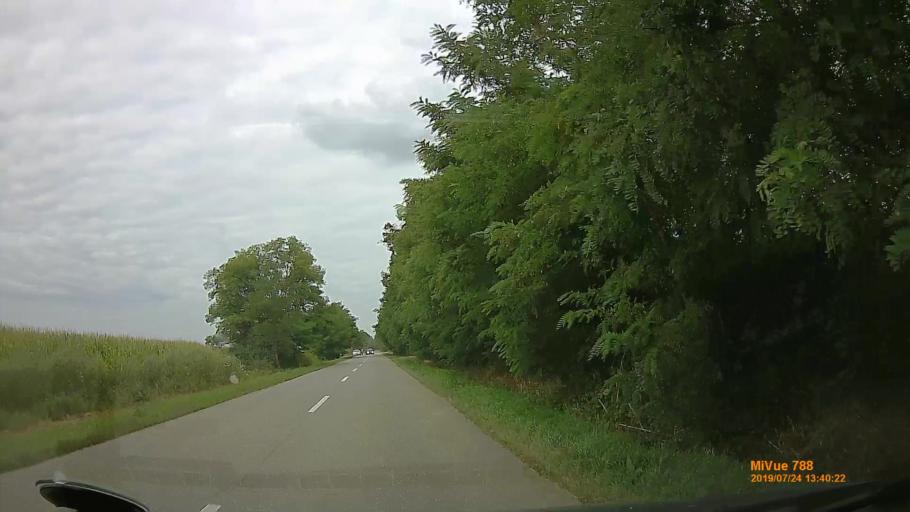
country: HU
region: Szabolcs-Szatmar-Bereg
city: Aranyosapati
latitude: 48.2508
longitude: 22.3152
